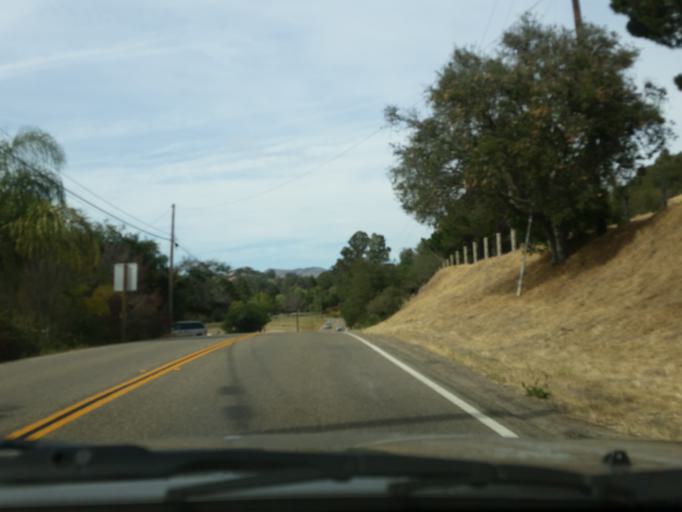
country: US
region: California
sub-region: San Luis Obispo County
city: Arroyo Grande
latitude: 35.1303
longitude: -120.5715
